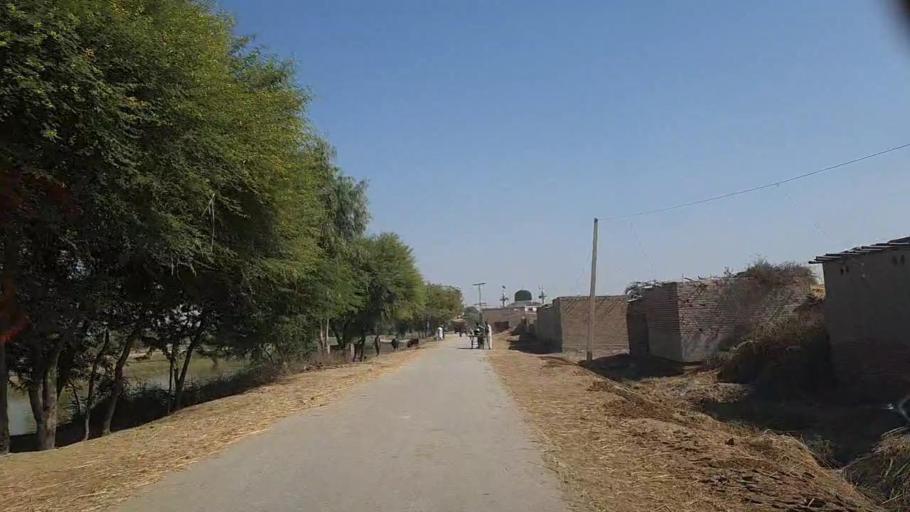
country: PK
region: Sindh
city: Thul
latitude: 28.2448
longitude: 68.8033
